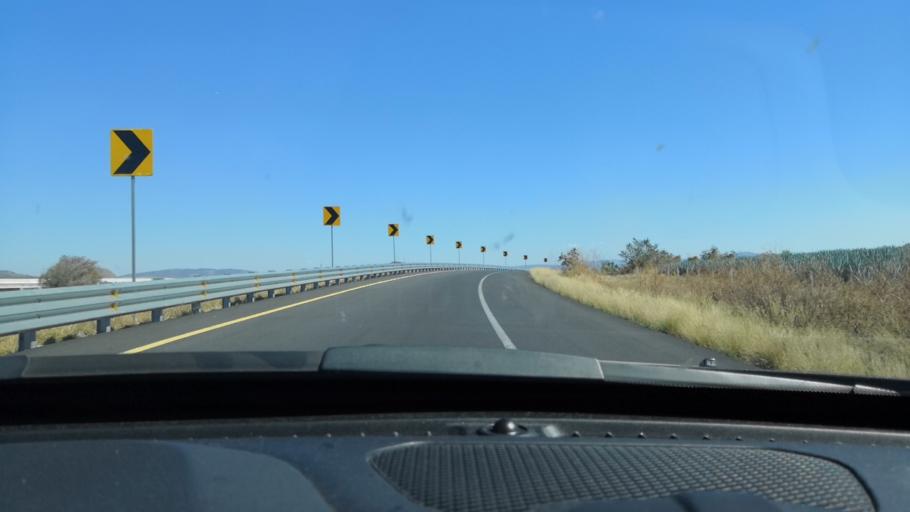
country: MX
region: Jalisco
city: Arenal
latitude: 20.7944
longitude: -103.7143
